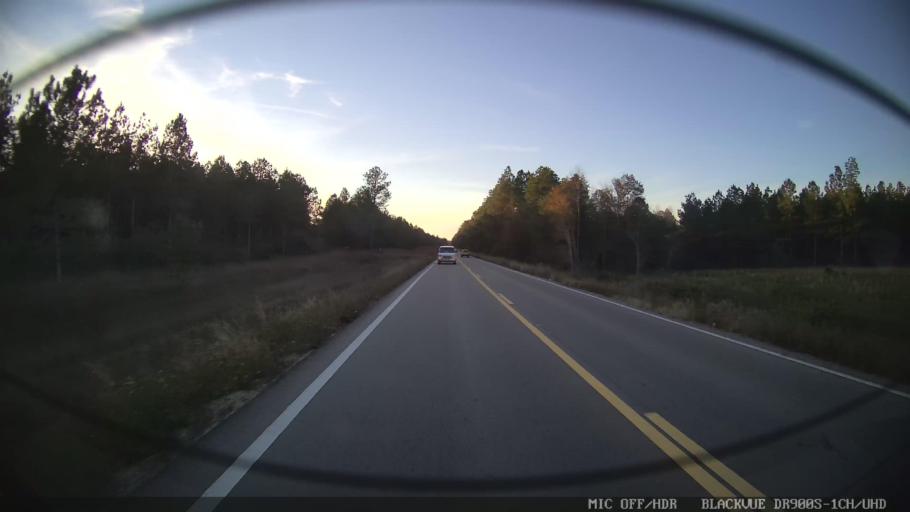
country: US
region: Mississippi
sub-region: Lamar County
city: Lumberton
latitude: 30.9936
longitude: -89.2856
